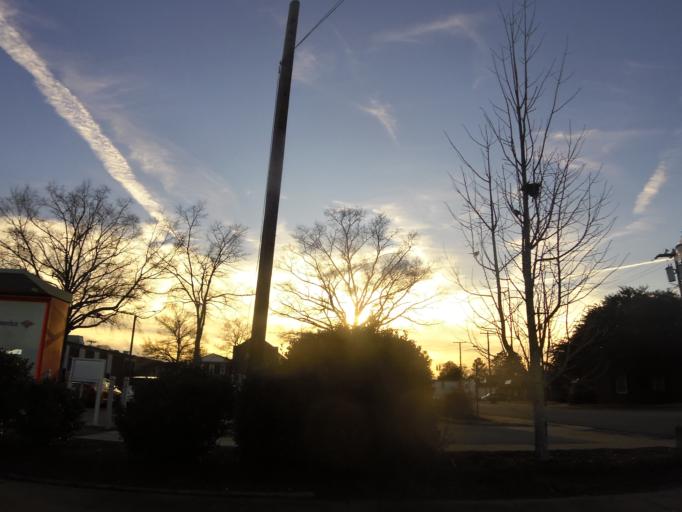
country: US
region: Virginia
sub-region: City of Franklin
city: Franklin
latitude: 36.6793
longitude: -76.9229
